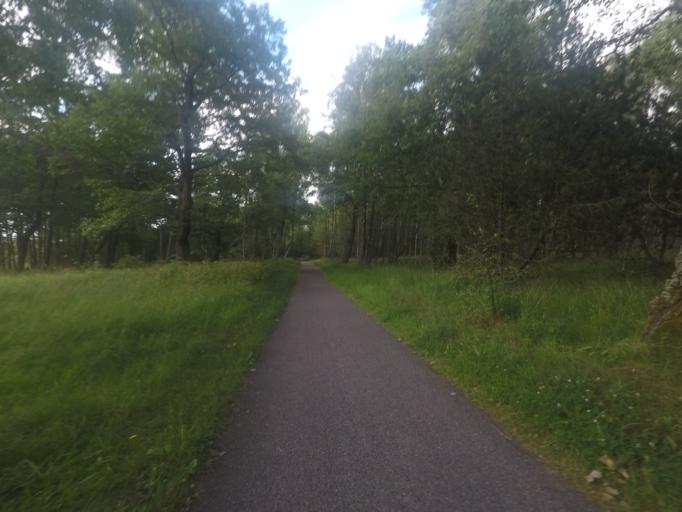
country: LT
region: Klaipedos apskritis
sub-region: Klaipeda
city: Klaipeda
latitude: 55.6488
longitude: 21.1080
